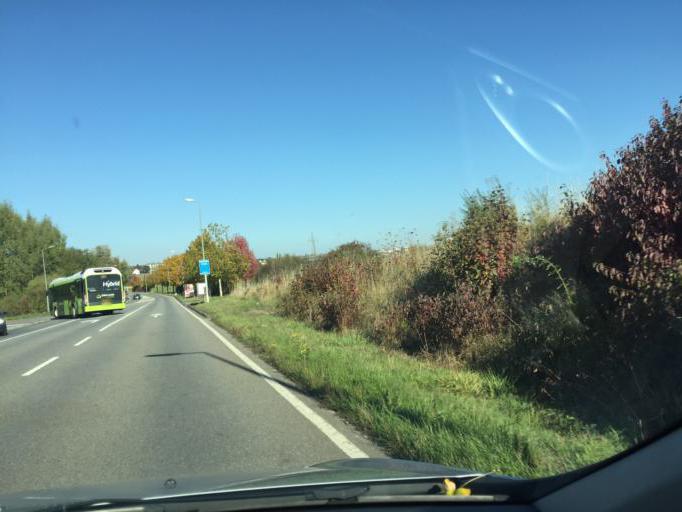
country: LU
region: Luxembourg
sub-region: Canton de Luxembourg
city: Bertrange
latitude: 49.6010
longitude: 6.0558
